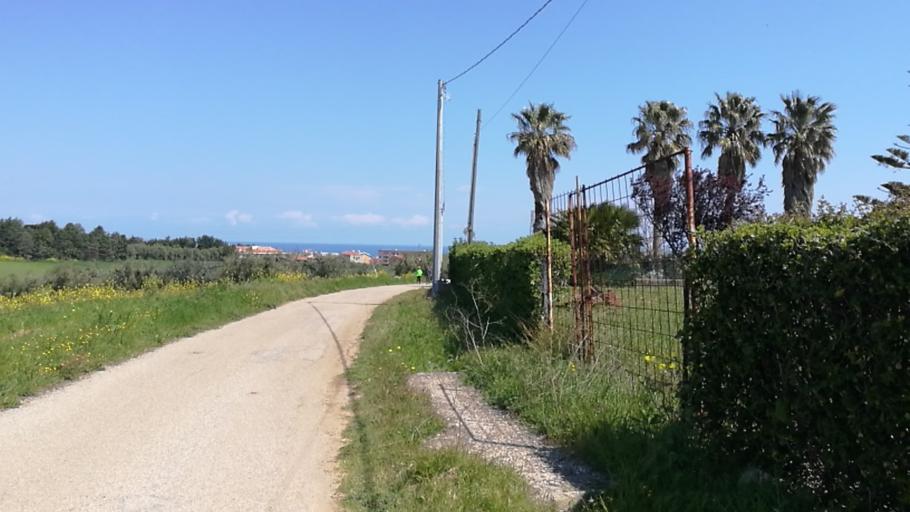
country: IT
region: Molise
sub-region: Provincia di Campobasso
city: Termoli
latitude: 41.9733
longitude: 14.9832
